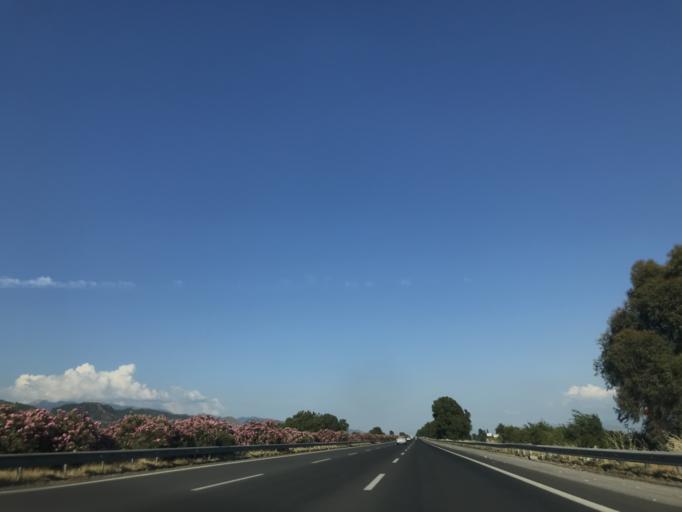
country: TR
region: Aydin
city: Germencik
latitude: 37.8701
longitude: 27.6427
